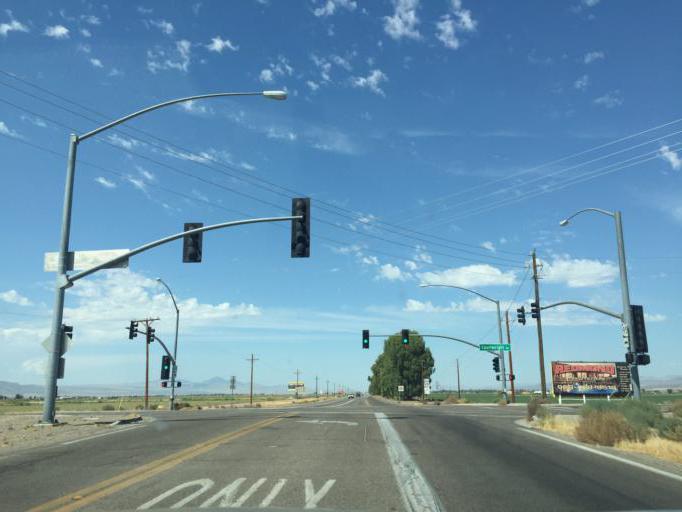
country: US
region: California
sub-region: San Bernardino County
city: Needles
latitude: 34.8658
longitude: -114.5977
